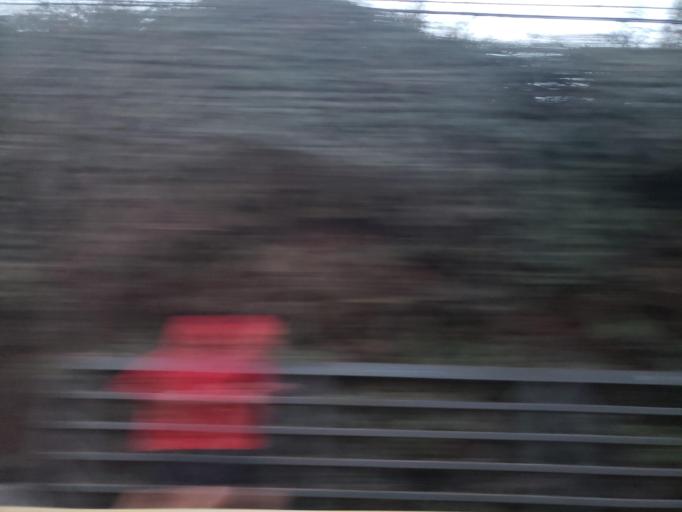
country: CL
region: Santiago Metropolitan
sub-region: Provincia de Talagante
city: Talagante
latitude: -33.6772
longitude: -70.9545
